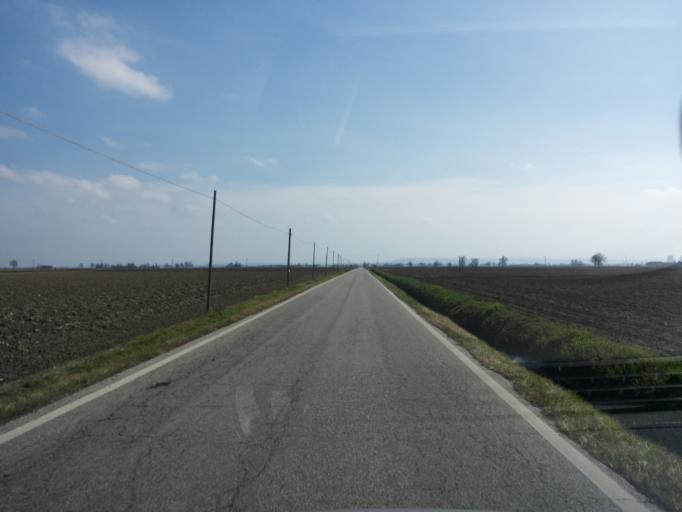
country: IT
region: Piedmont
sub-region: Provincia di Vercelli
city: Crova
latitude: 45.3187
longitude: 8.1966
